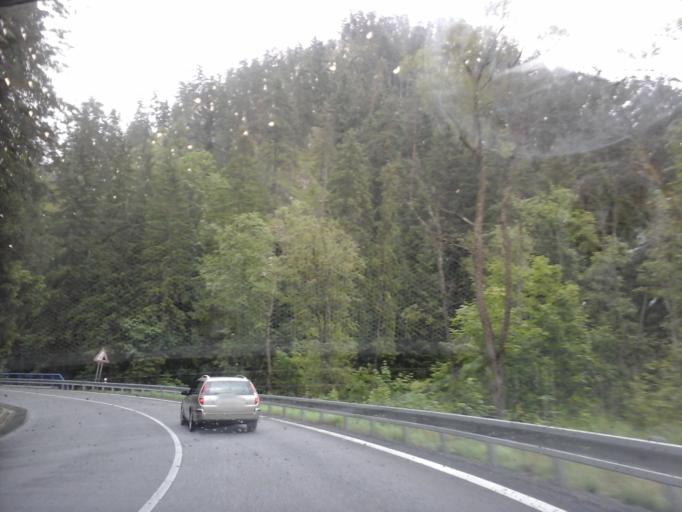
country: SK
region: Presovsky
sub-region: Okres Poprad
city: Poprad
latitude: 48.9311
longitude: 20.2858
